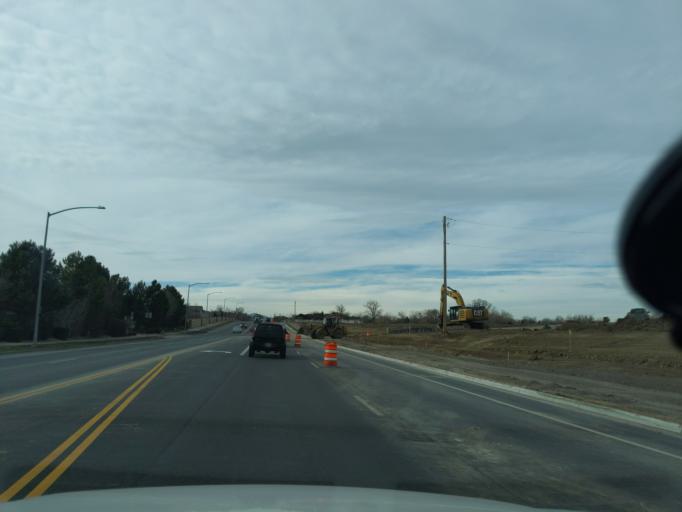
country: US
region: Colorado
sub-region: Adams County
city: Thornton
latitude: 39.8995
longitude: -104.9506
